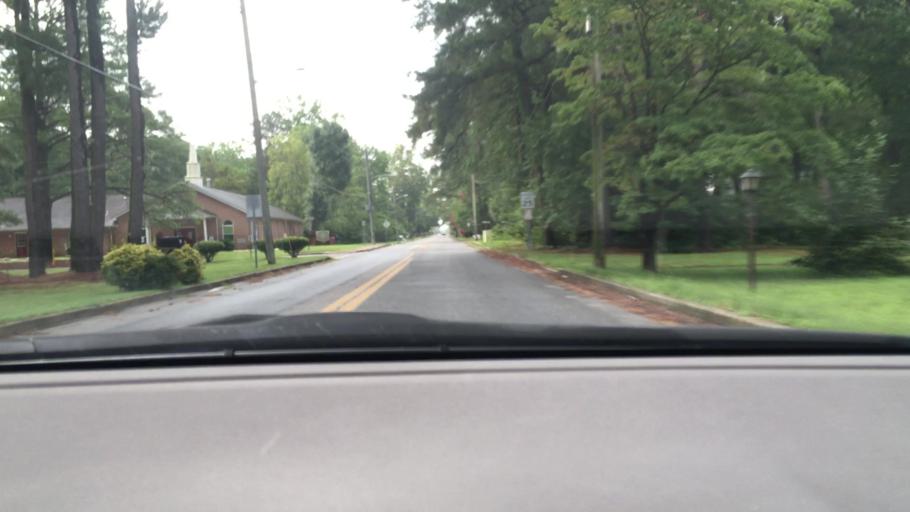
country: US
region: Maryland
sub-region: Wicomico County
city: Fruitland
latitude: 38.3321
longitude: -75.6266
